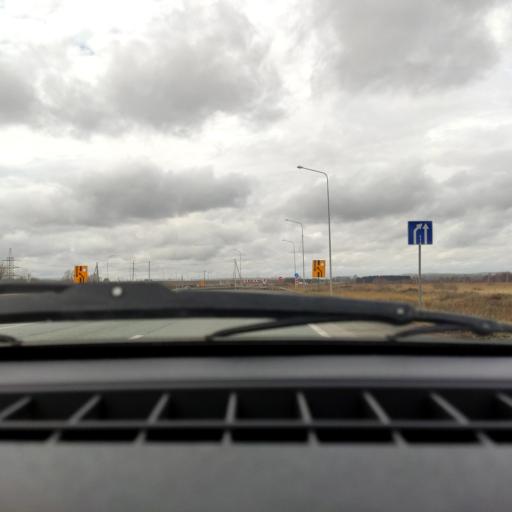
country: RU
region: Bashkortostan
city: Asanovo
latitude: 54.9096
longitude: 55.6018
